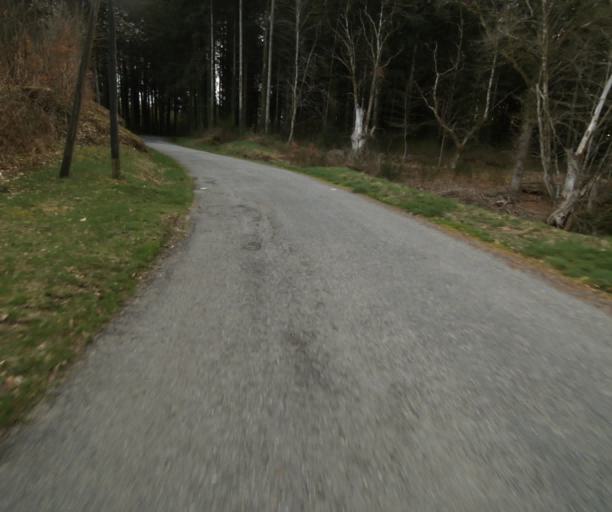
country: FR
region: Limousin
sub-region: Departement de la Correze
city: Argentat
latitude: 45.2209
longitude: 1.9630
